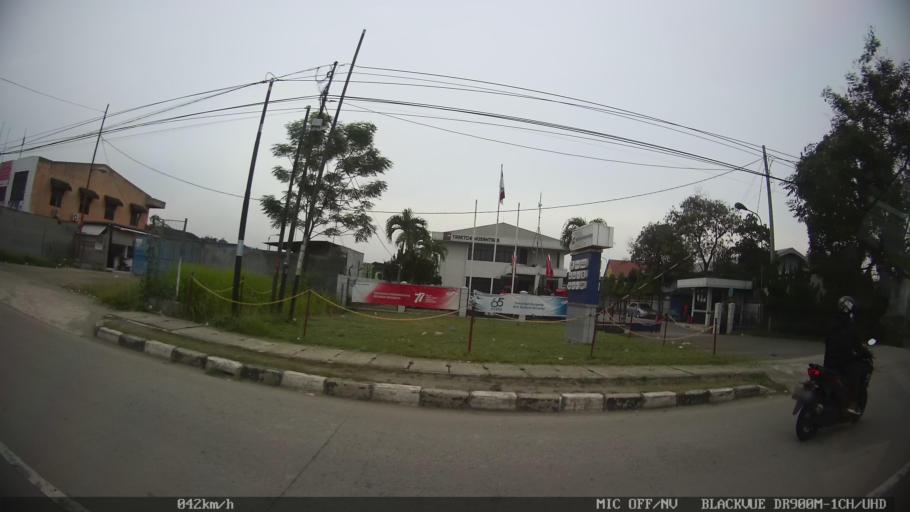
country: ID
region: North Sumatra
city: Deli Tua
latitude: 3.5325
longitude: 98.7288
